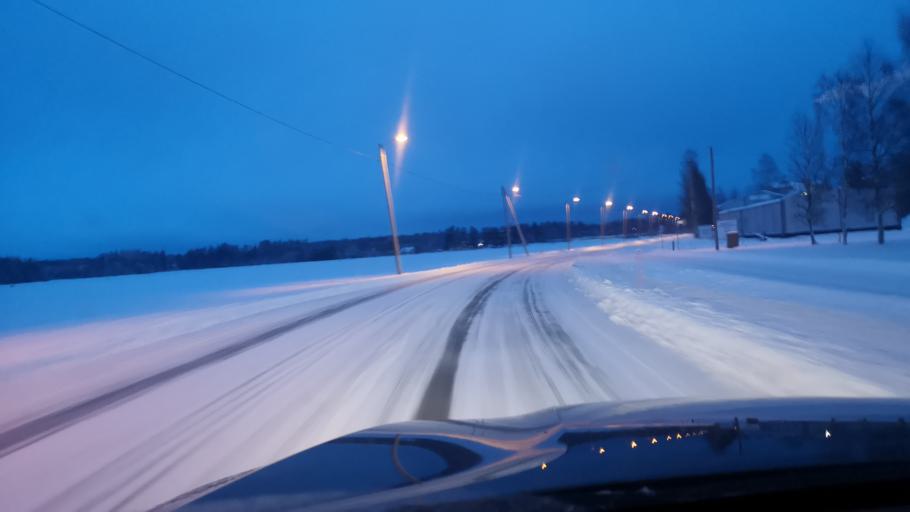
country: FI
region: Varsinais-Suomi
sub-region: Loimaa
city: Loimaa
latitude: 60.8588
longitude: 23.0675
